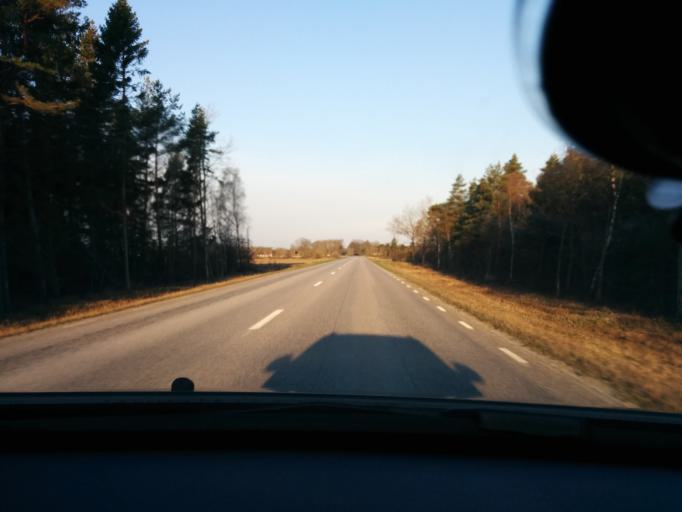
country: SE
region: Gotland
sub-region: Gotland
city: Visby
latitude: 57.6394
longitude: 18.4893
